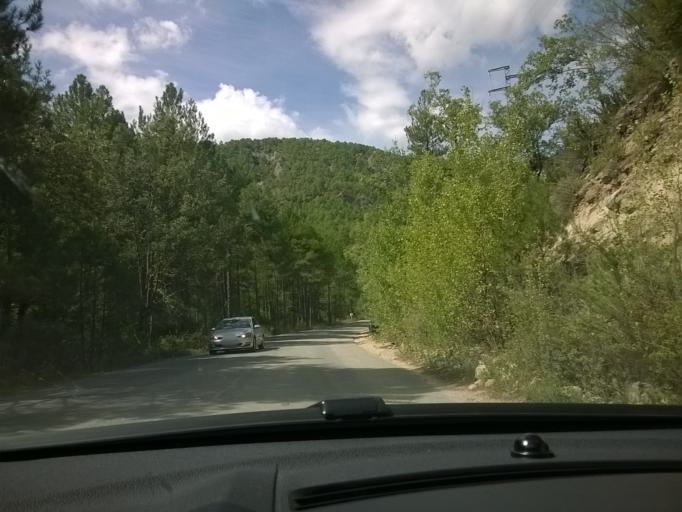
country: ES
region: Castille-La Mancha
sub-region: Provincia de Cuenca
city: Fuertescusa
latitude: 40.5067
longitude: -2.1331
